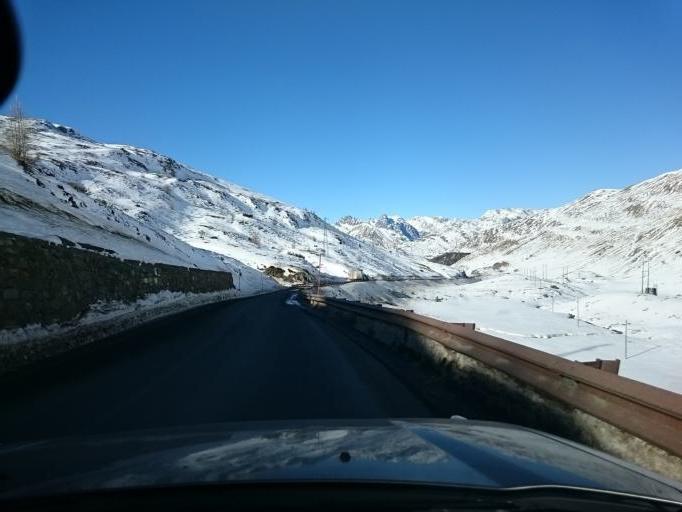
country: IT
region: Lombardy
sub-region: Provincia di Sondrio
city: Livigno
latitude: 46.4999
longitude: 10.2045
